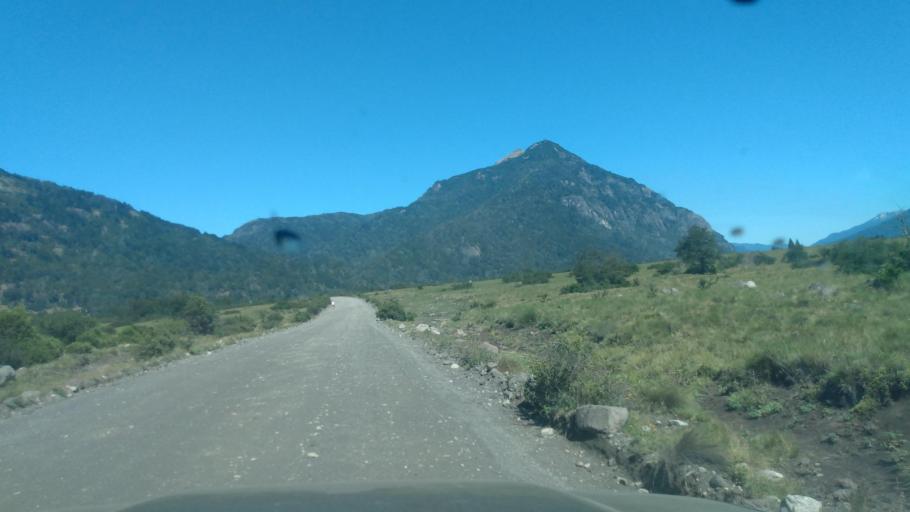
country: AR
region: Neuquen
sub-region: Departamento de Lacar
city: San Martin de los Andes
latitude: -39.7461
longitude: -71.5074
